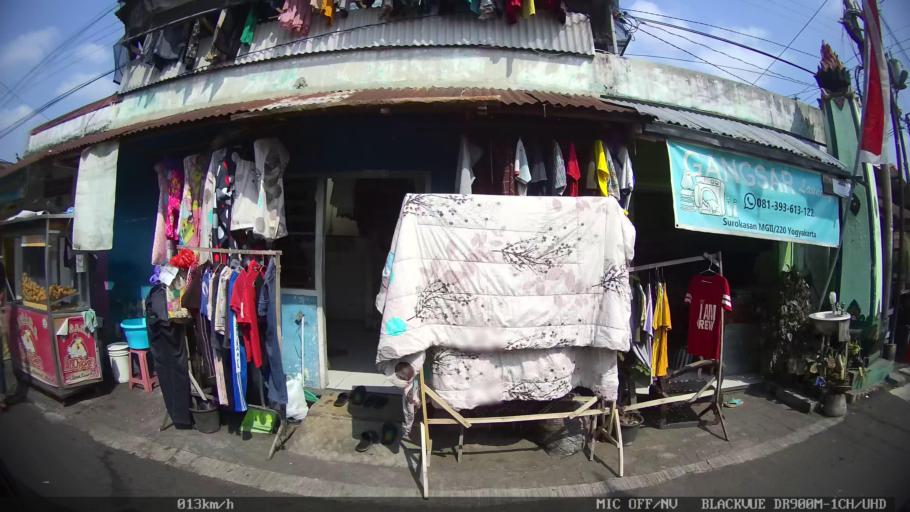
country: ID
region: Daerah Istimewa Yogyakarta
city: Yogyakarta
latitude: -7.8044
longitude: 110.3753
